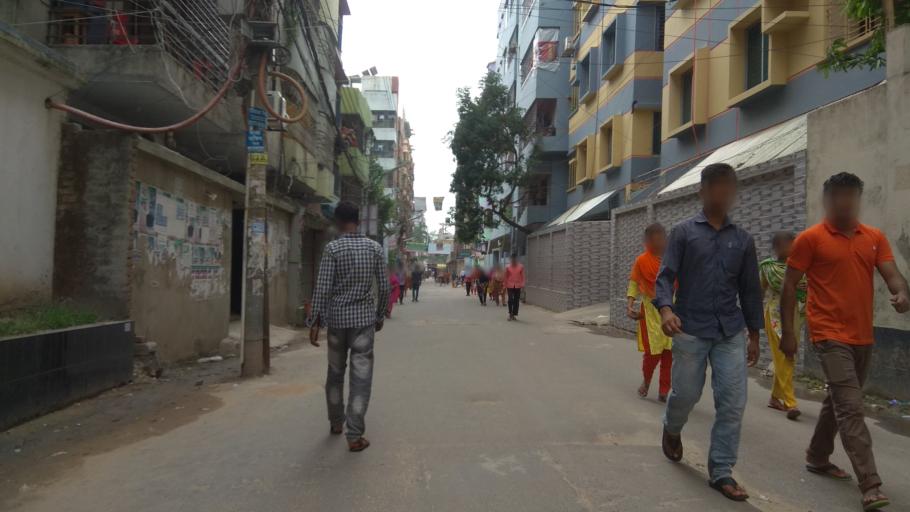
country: BD
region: Dhaka
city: Tungi
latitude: 23.8198
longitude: 90.3582
